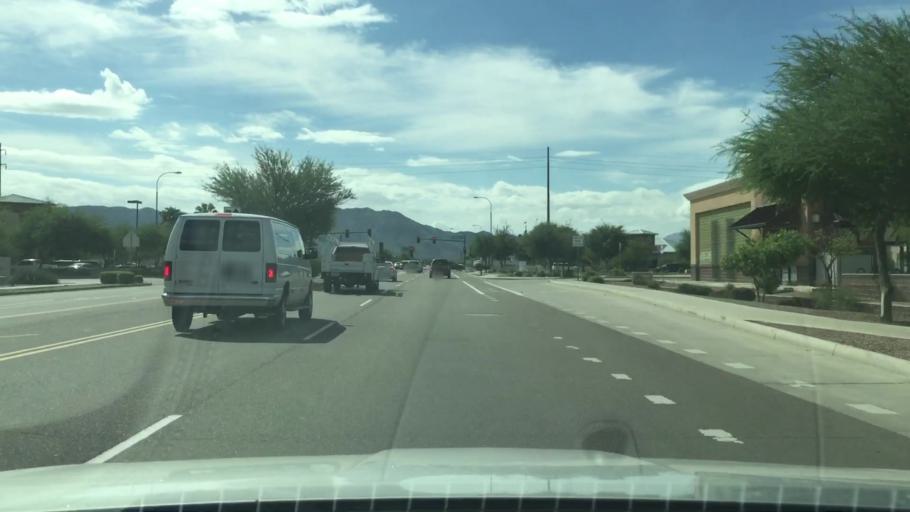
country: US
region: Arizona
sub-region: Maricopa County
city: Laveen
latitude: 33.3936
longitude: -112.1337
